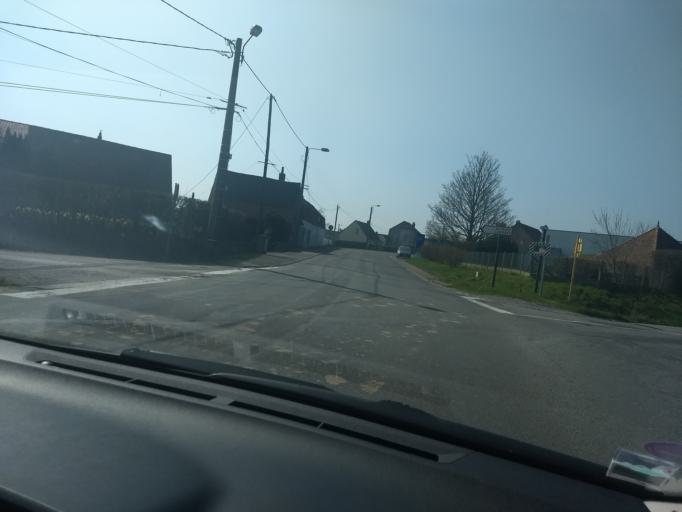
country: FR
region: Nord-Pas-de-Calais
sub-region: Departement du Pas-de-Calais
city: Tatinghem
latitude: 50.7409
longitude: 2.2024
